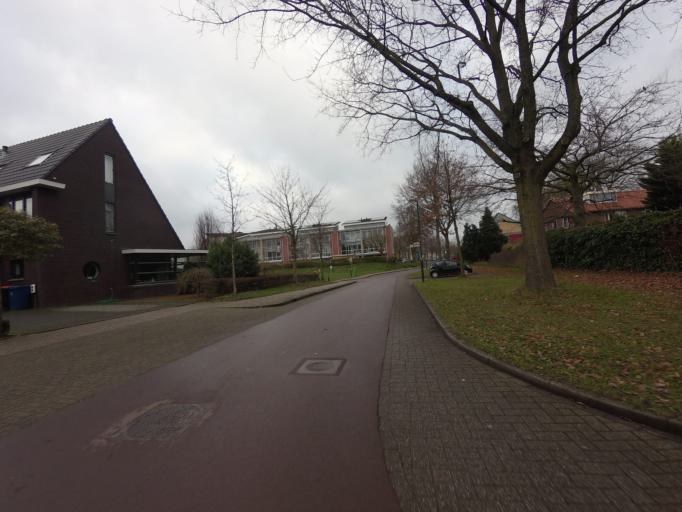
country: NL
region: Utrecht
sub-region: Gemeente Houten
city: Houten
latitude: 52.0254
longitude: 5.1606
